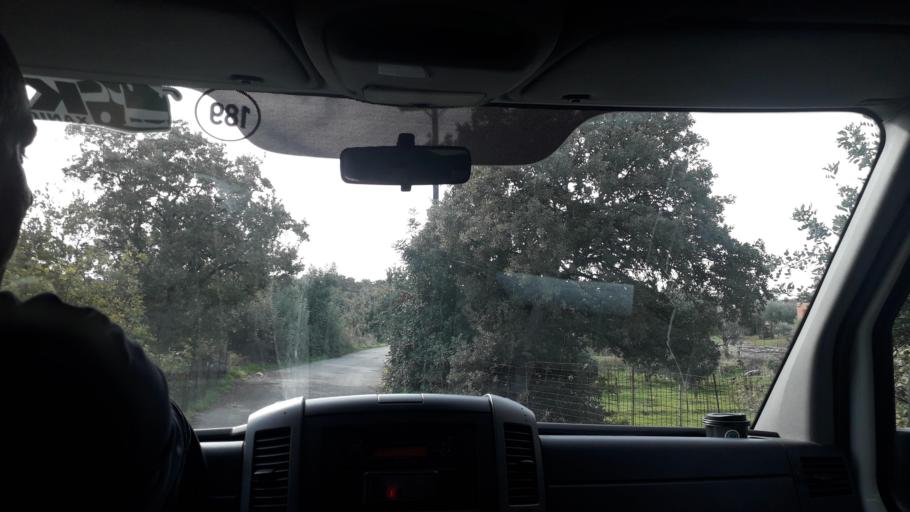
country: GR
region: Crete
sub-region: Nomos Rethymnis
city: Atsipopoulon
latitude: 35.3588
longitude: 24.4321
